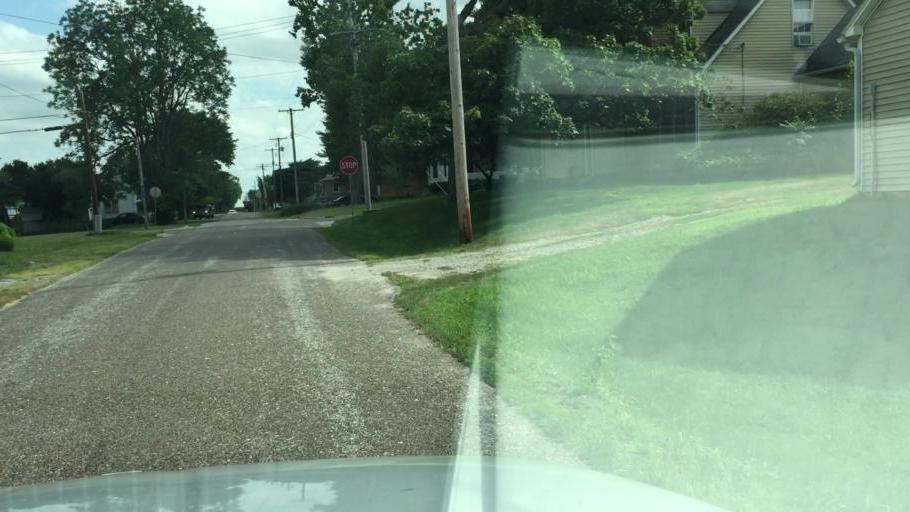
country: US
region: Illinois
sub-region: Hancock County
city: Carthage
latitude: 40.4141
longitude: -91.1275
